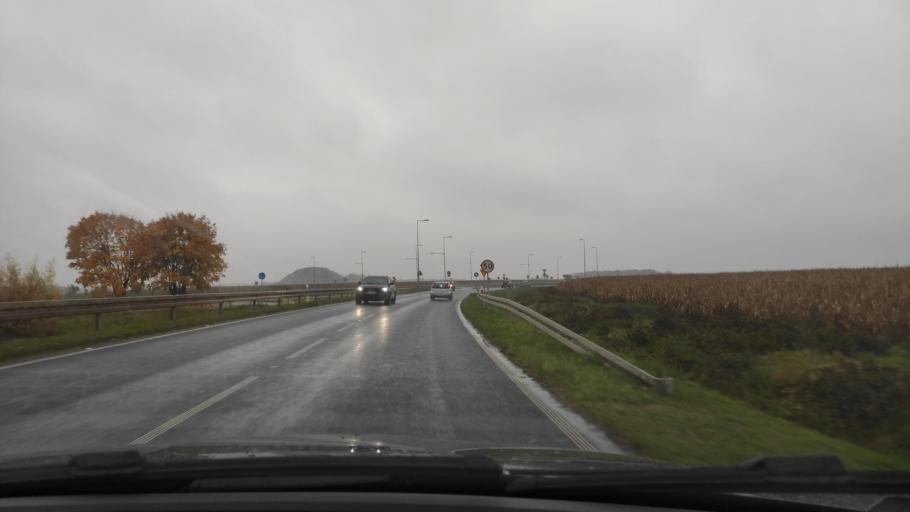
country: PL
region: Greater Poland Voivodeship
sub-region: Powiat poznanski
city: Swarzedz
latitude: 52.3311
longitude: 17.0530
